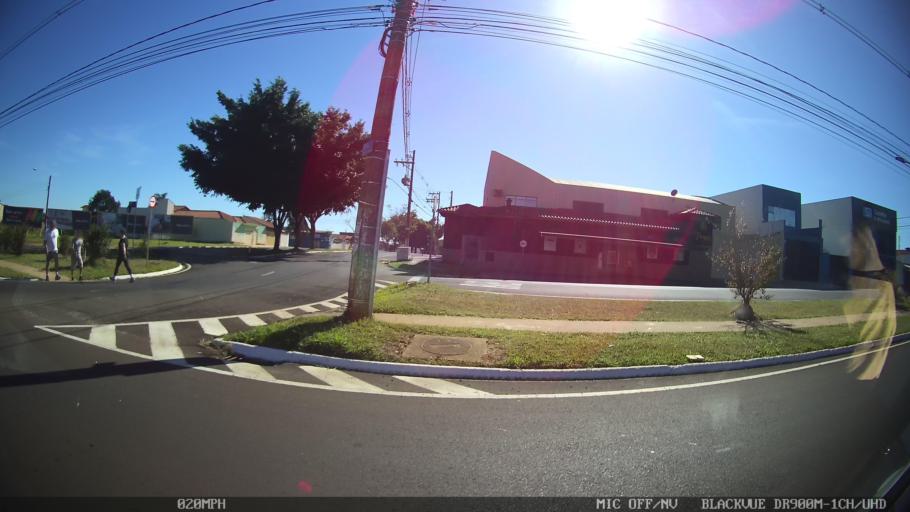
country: BR
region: Sao Paulo
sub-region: Franca
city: Franca
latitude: -20.5606
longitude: -47.3730
